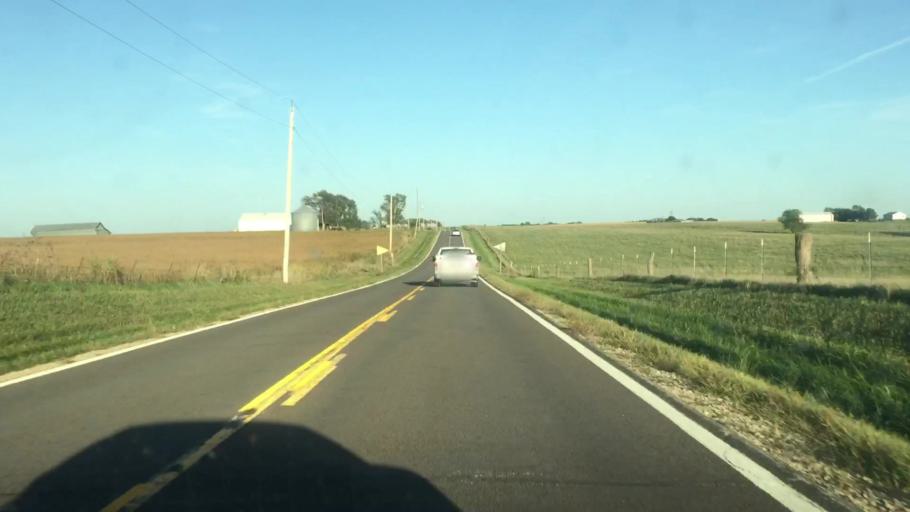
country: US
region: Kansas
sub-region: Brown County
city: Horton
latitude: 39.5516
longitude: -95.4470
